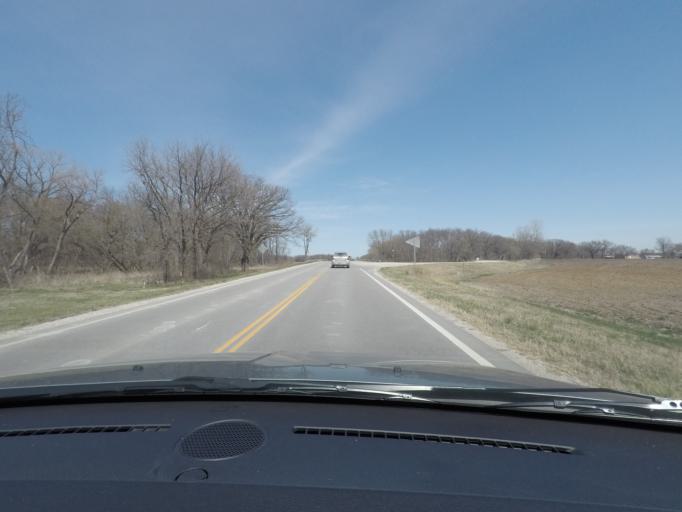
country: US
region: Kansas
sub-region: Lyon County
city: Emporia
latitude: 38.4606
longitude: -96.1710
